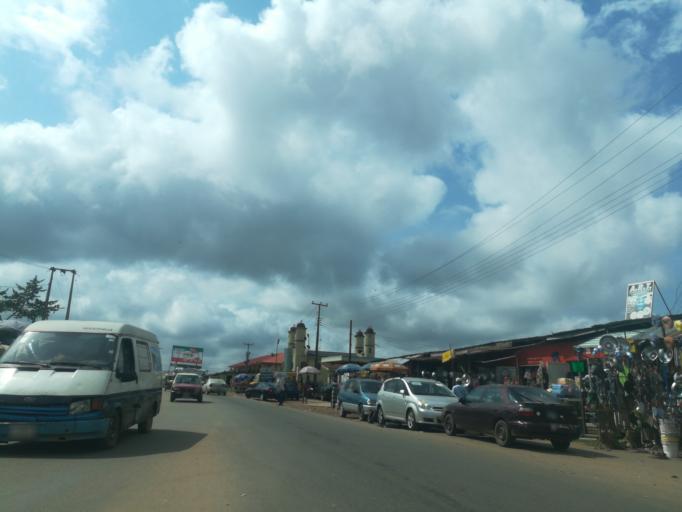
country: NG
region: Oyo
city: Ibadan
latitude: 7.3311
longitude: 3.8678
